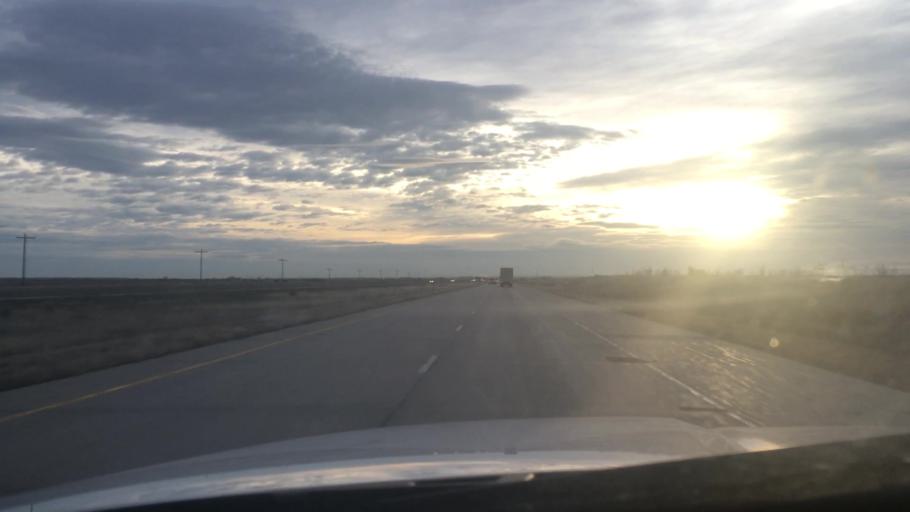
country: US
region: Colorado
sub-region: Morgan County
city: Fort Morgan
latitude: 40.2495
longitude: -104.0098
